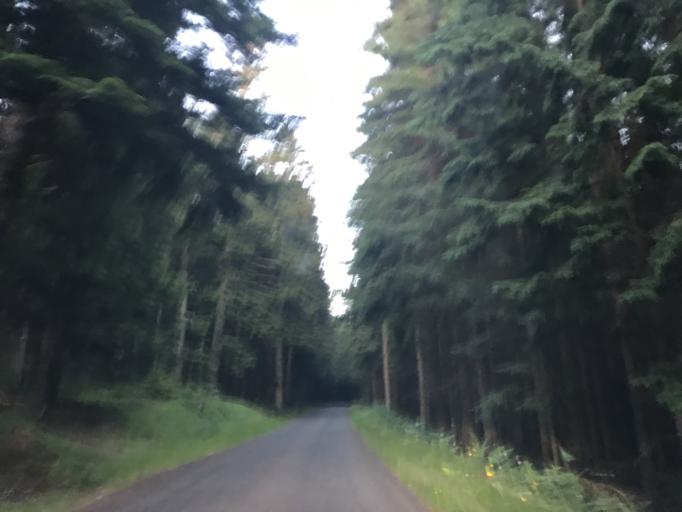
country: FR
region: Rhone-Alpes
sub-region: Departement de la Loire
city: Noiretable
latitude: 45.7655
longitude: 3.7183
